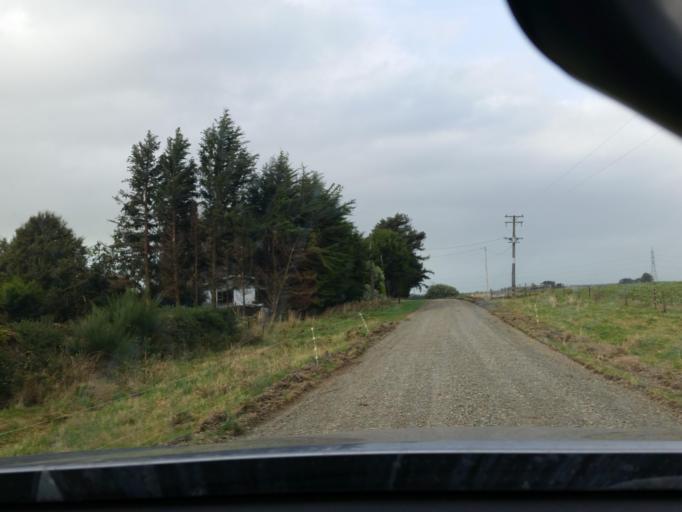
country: NZ
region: Southland
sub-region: Invercargill City
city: Invercargill
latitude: -46.3366
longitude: 168.3800
